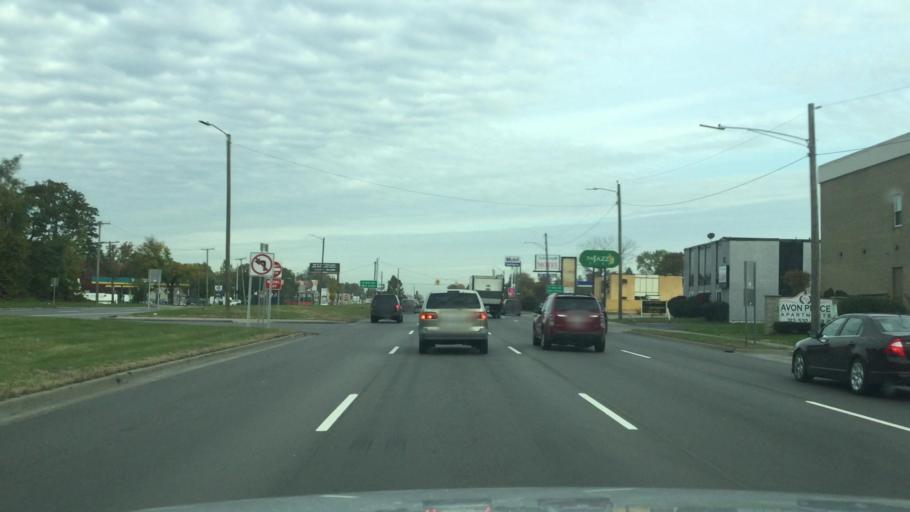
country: US
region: Michigan
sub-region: Wayne County
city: Redford
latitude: 42.4125
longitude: -83.2769
